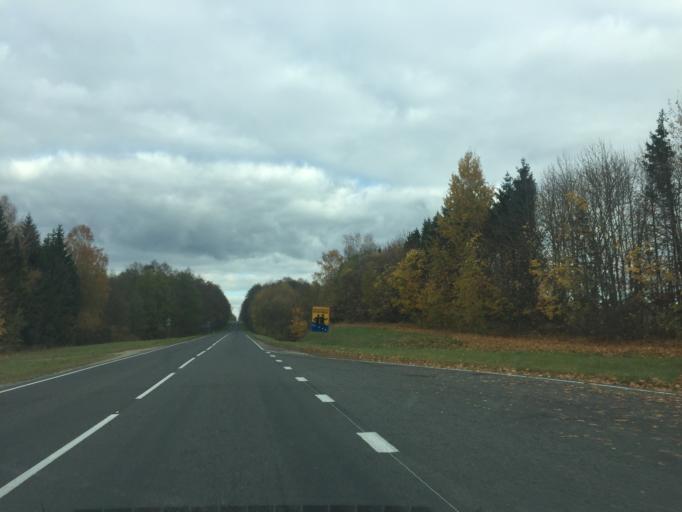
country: BY
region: Minsk
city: Svir
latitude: 54.8968
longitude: 26.4052
